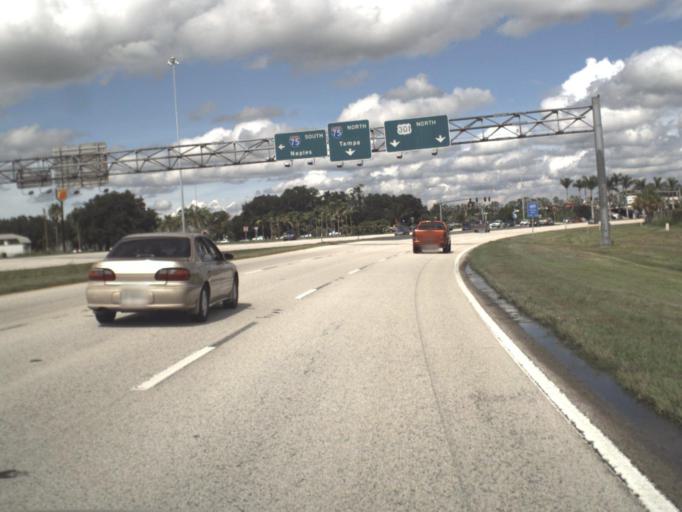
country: US
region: Florida
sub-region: Manatee County
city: Ellenton
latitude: 27.5275
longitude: -82.5117
